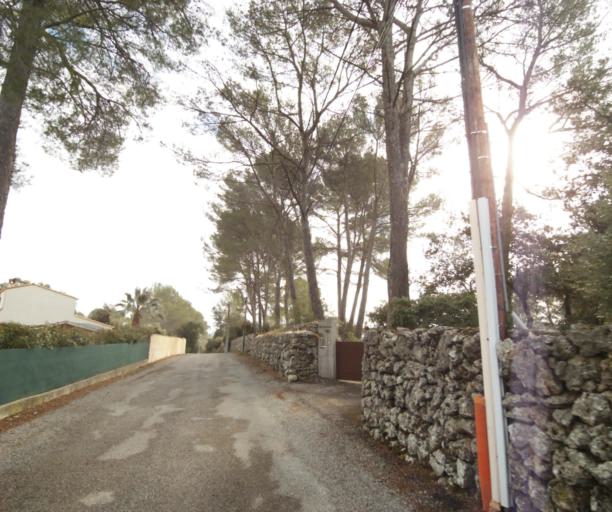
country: FR
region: Provence-Alpes-Cote d'Azur
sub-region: Departement du Var
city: Trans-en-Provence
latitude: 43.5049
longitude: 6.4983
